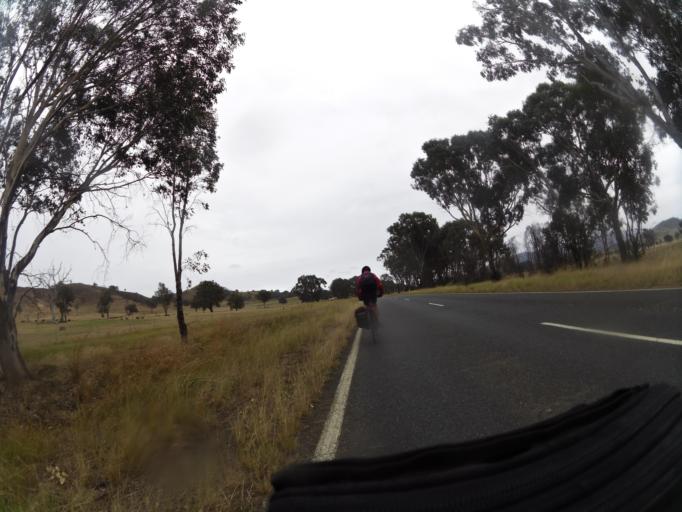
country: AU
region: New South Wales
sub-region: Greater Hume Shire
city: Holbrook
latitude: -36.2151
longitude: 147.8254
